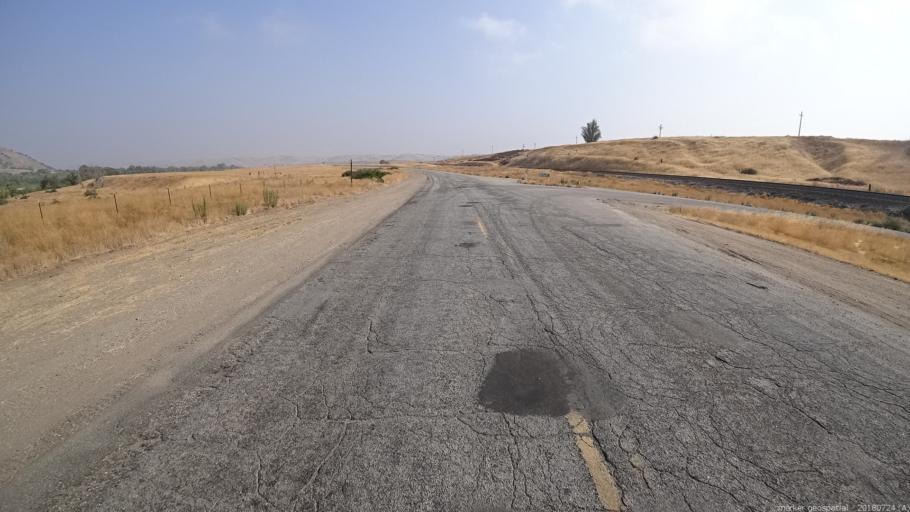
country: US
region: California
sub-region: San Luis Obispo County
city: San Miguel
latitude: 35.8268
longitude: -120.7508
